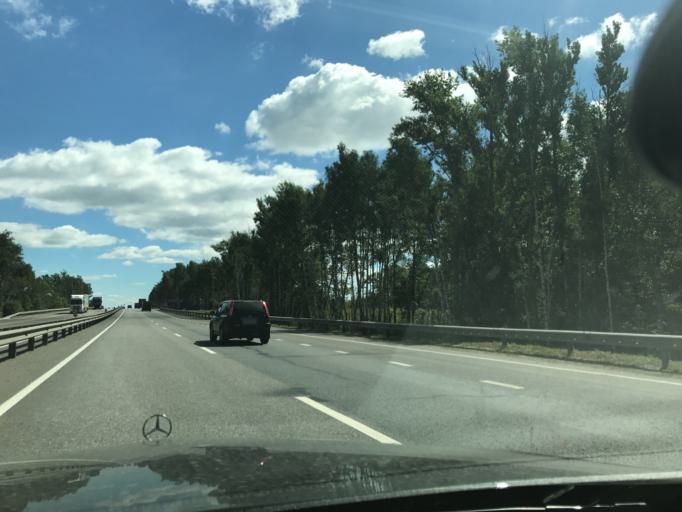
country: RU
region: Vladimir
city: Novovyazniki
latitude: 56.1985
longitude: 42.3643
